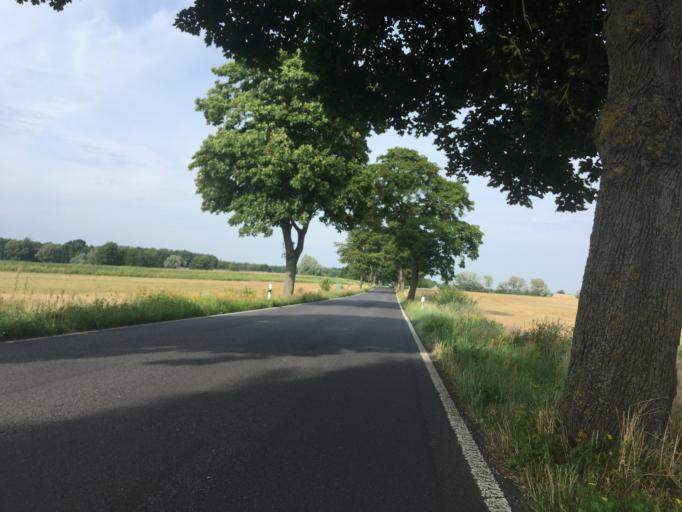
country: DE
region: Brandenburg
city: Eberswalde
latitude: 52.7625
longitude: 13.8122
